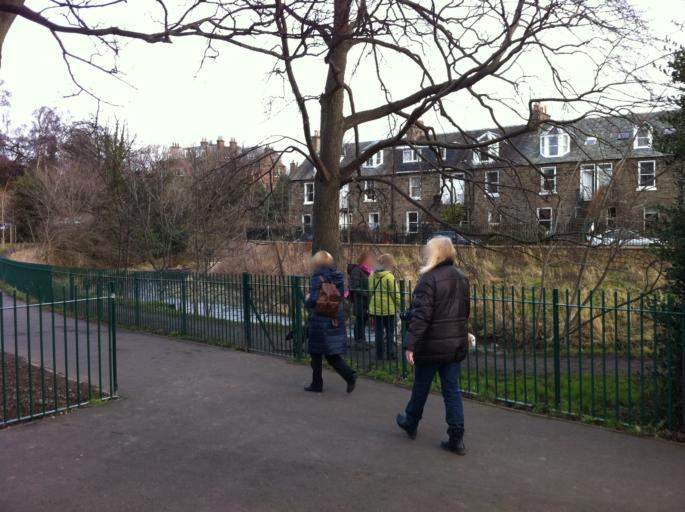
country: GB
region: Scotland
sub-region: Edinburgh
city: Edinburgh
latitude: 55.9613
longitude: -3.2121
